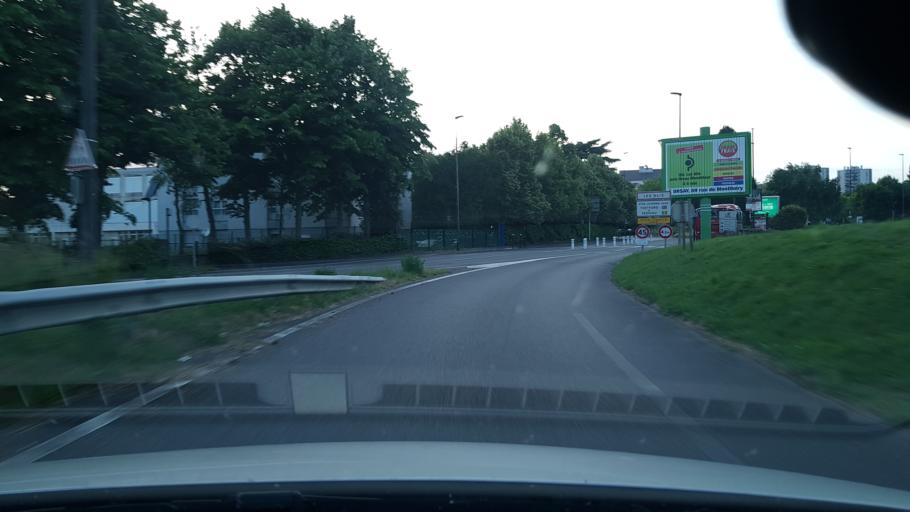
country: FR
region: Ile-de-France
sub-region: Departement de l'Essonne
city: Les Ulis
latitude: 48.6755
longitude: 2.1675
